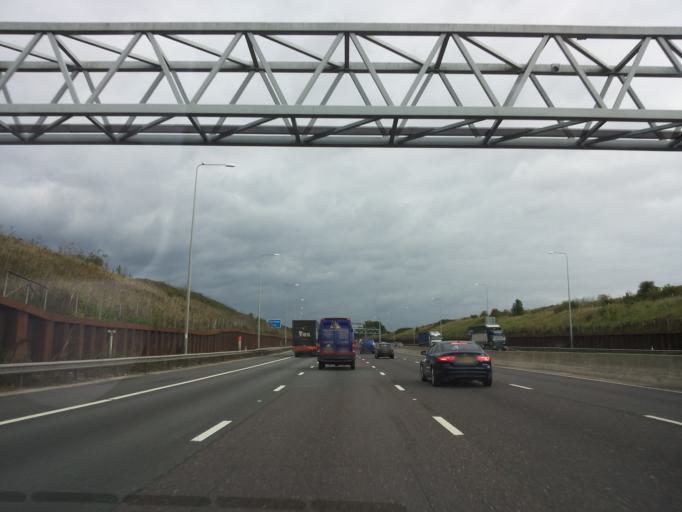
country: GB
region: England
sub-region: Hertfordshire
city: Radlett
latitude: 51.7101
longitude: -0.3522
